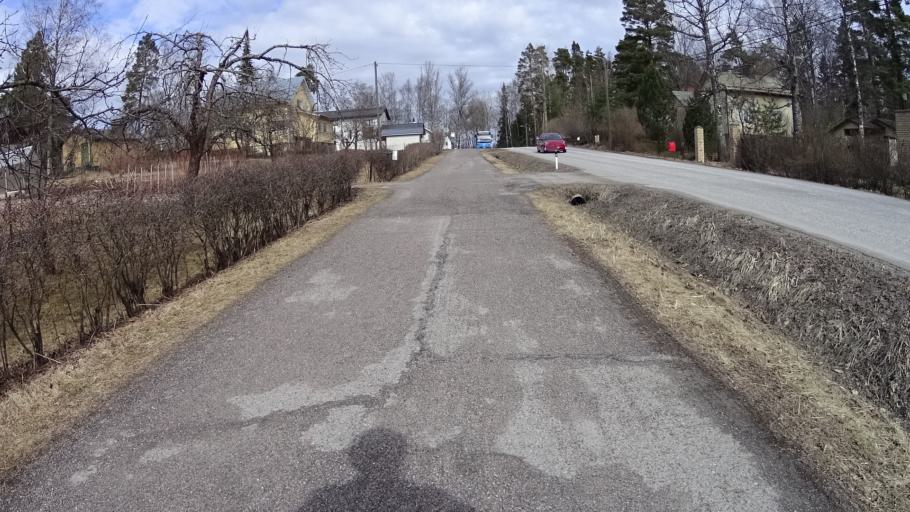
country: FI
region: Uusimaa
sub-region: Helsinki
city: Kilo
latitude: 60.2460
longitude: 24.8084
